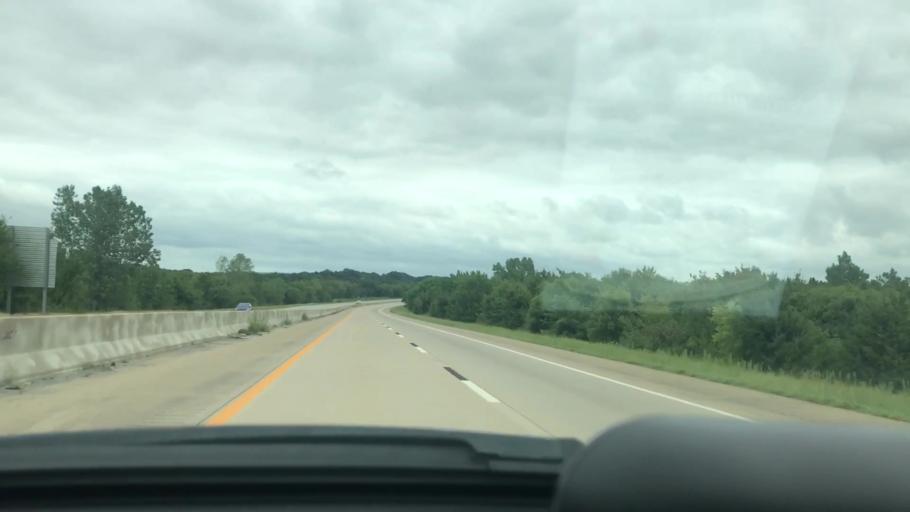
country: US
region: Oklahoma
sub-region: McIntosh County
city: Eufaula
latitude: 35.1885
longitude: -95.6394
